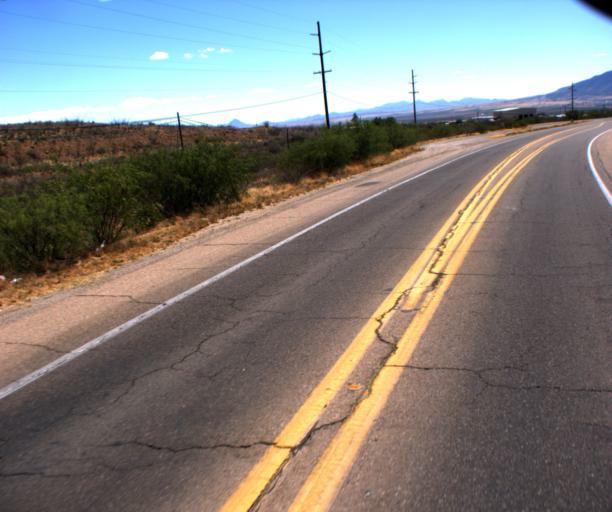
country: US
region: Arizona
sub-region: Cochise County
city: Bisbee
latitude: 31.4098
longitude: -109.9012
